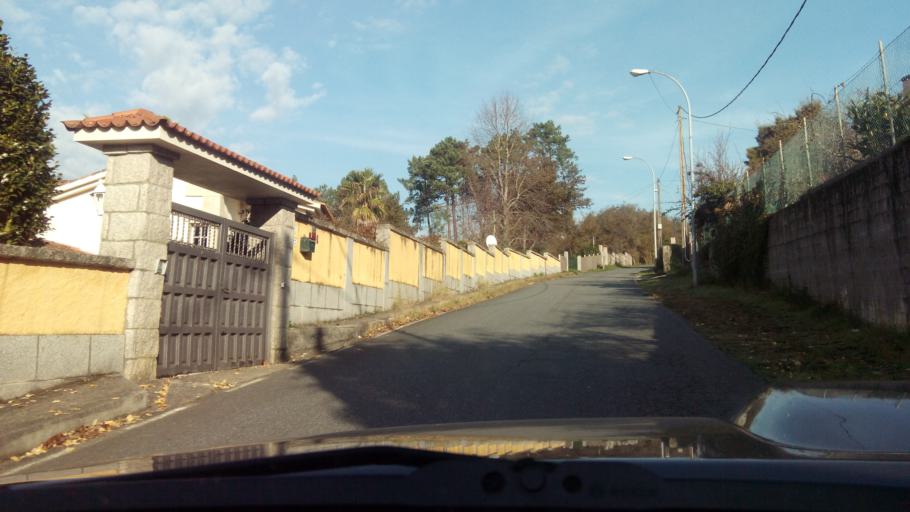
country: ES
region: Galicia
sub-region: Provincia de Pontevedra
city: Marin
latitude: 42.3778
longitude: -8.7266
